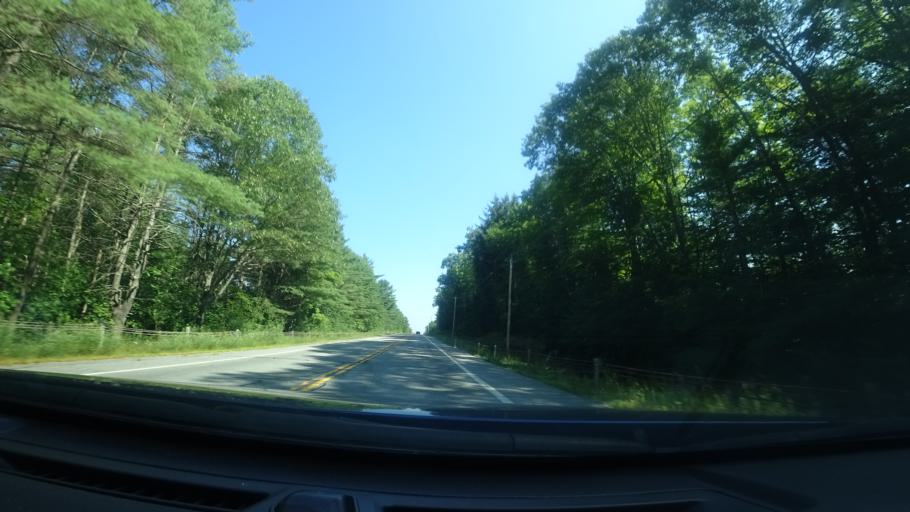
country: US
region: New York
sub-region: Warren County
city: Warrensburg
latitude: 43.6093
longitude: -73.8034
